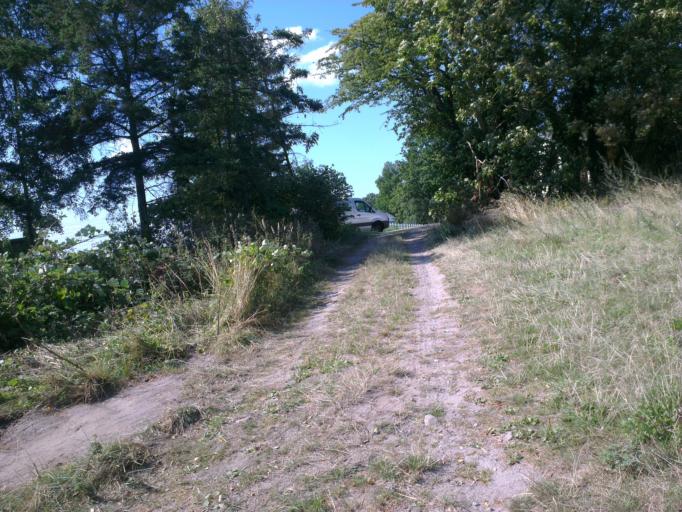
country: DK
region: Capital Region
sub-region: Frederikssund Kommune
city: Frederikssund
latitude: 55.8815
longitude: 12.0727
